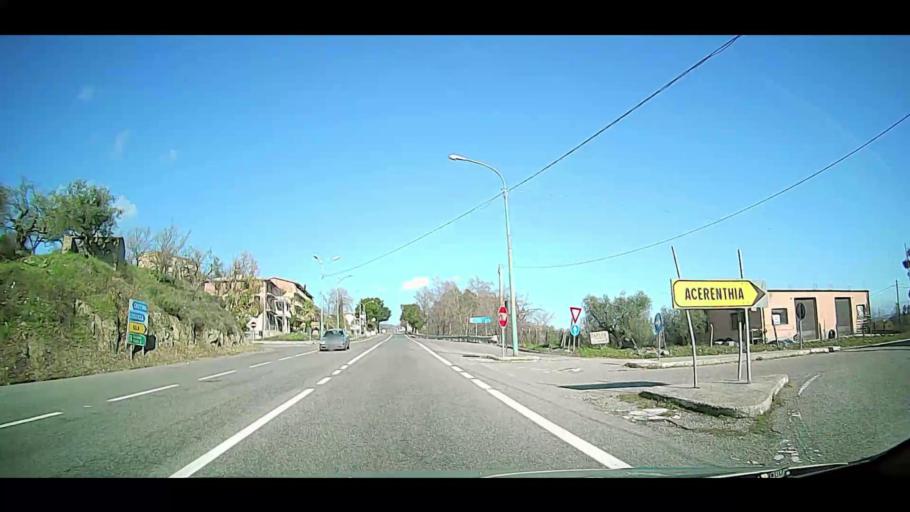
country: IT
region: Calabria
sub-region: Provincia di Crotone
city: Cerenzia
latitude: 39.2450
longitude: 16.7906
